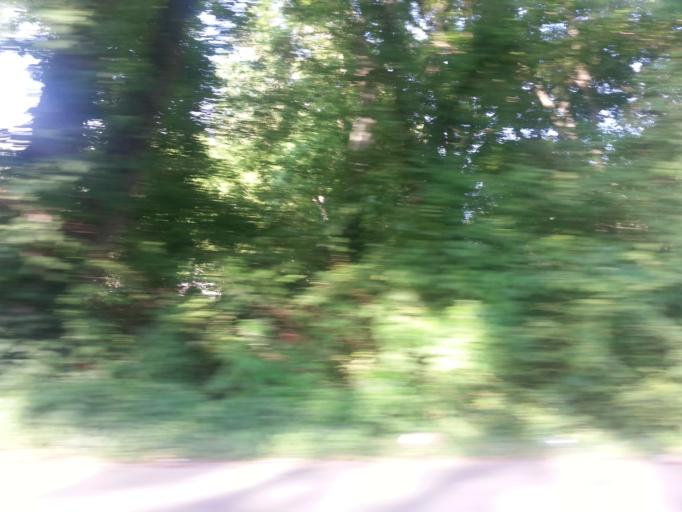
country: US
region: Tennessee
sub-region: Knox County
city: Knoxville
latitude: 35.9245
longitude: -83.9206
